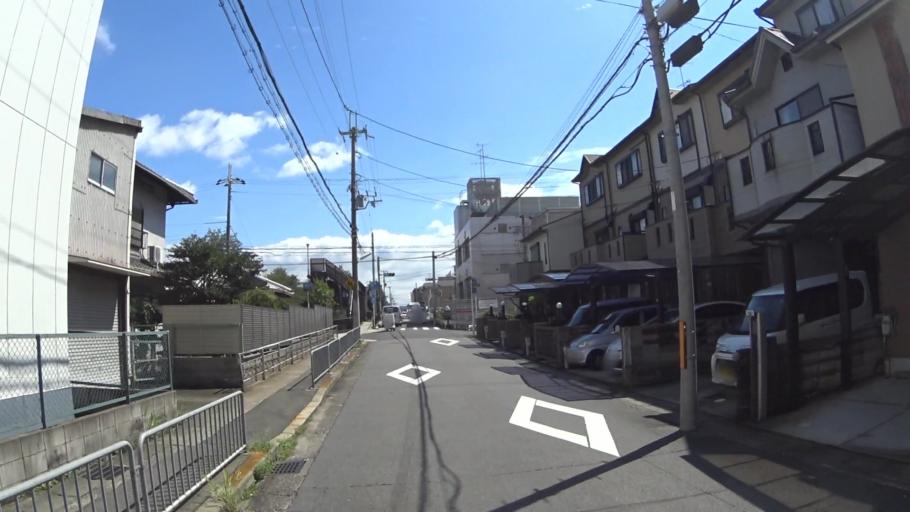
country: JP
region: Kyoto
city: Muko
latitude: 34.9976
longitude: 135.7157
